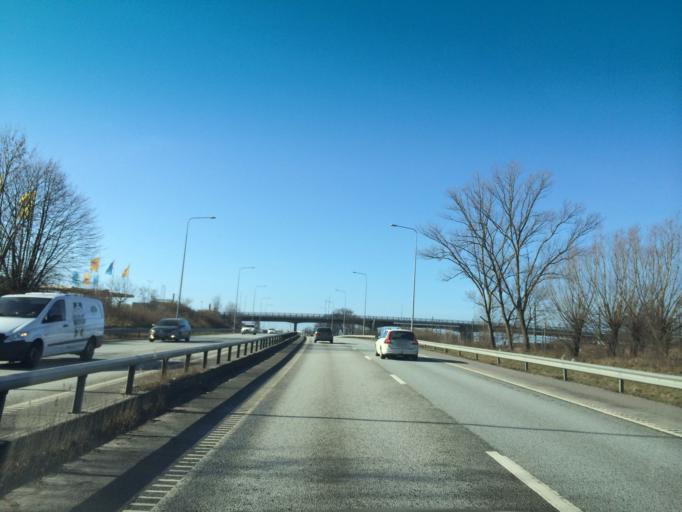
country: SE
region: Skane
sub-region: Burlovs Kommun
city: Arloev
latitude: 55.6164
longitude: 13.0450
